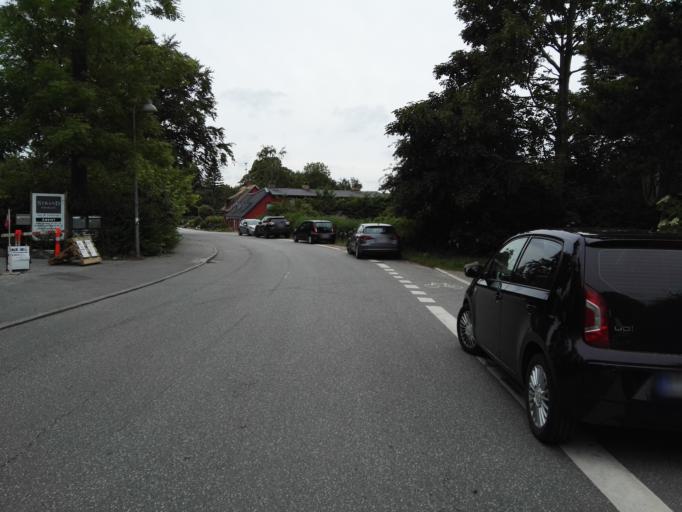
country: DK
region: Capital Region
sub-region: Egedal Kommune
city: Smorumnedre
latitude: 55.7353
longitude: 12.2714
